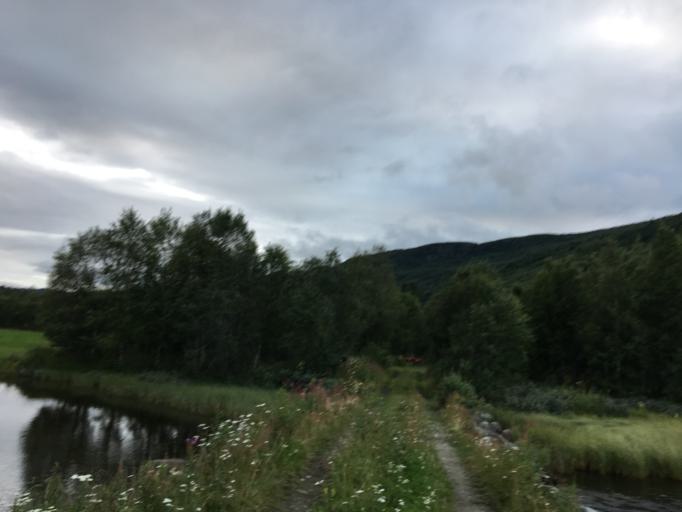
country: NO
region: Buskerud
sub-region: Hol
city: Hol
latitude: 60.6178
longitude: 8.2242
